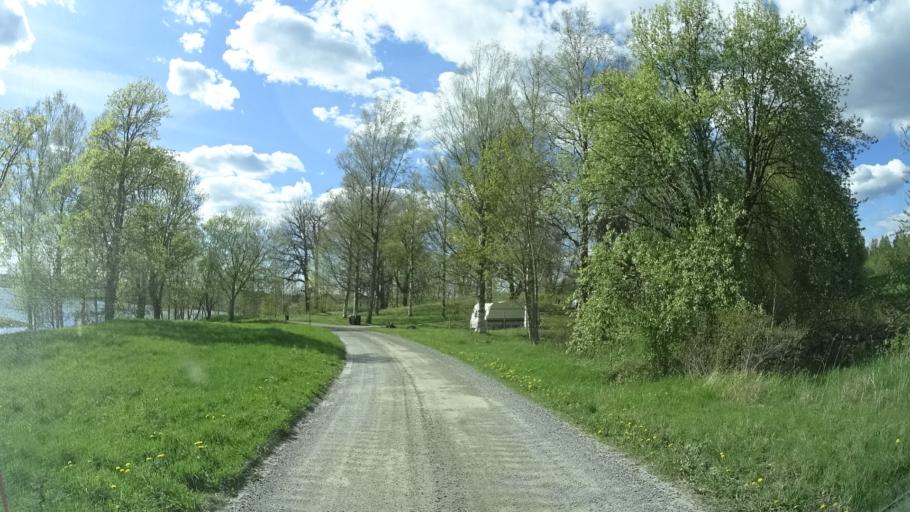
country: SE
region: OErebro
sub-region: Nora Kommun
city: As
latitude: 59.4456
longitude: 14.8133
